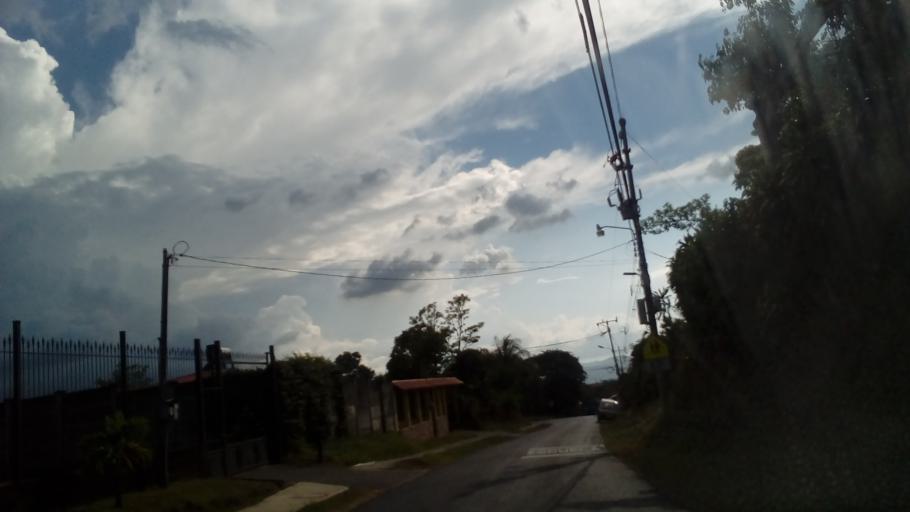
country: CR
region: Alajuela
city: San Juan
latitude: 10.0904
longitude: -84.2798
